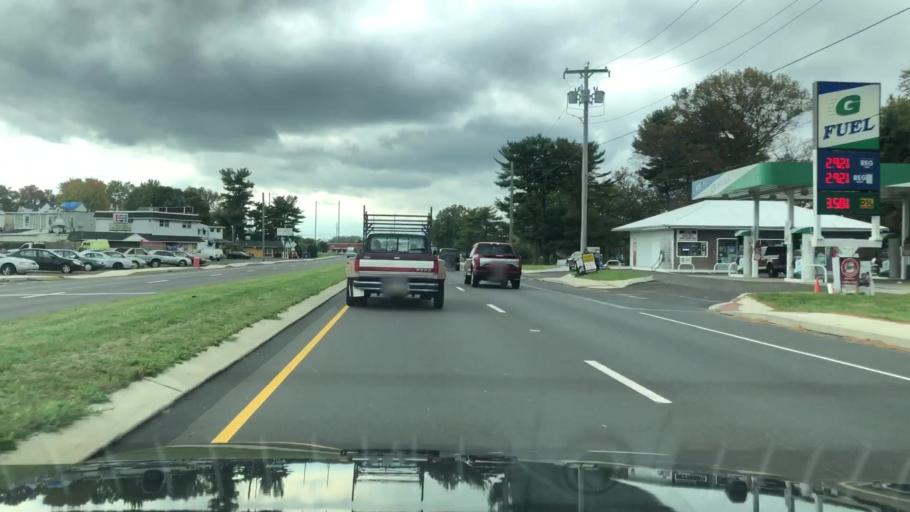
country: US
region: Pennsylvania
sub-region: Bucks County
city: Bristol
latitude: 40.1054
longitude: -74.8599
